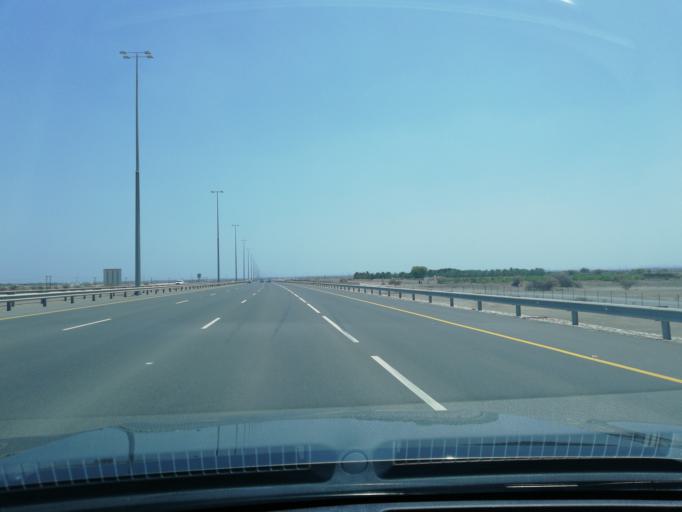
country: OM
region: Al Batinah
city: Barka'
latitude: 23.6209
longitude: 57.9358
